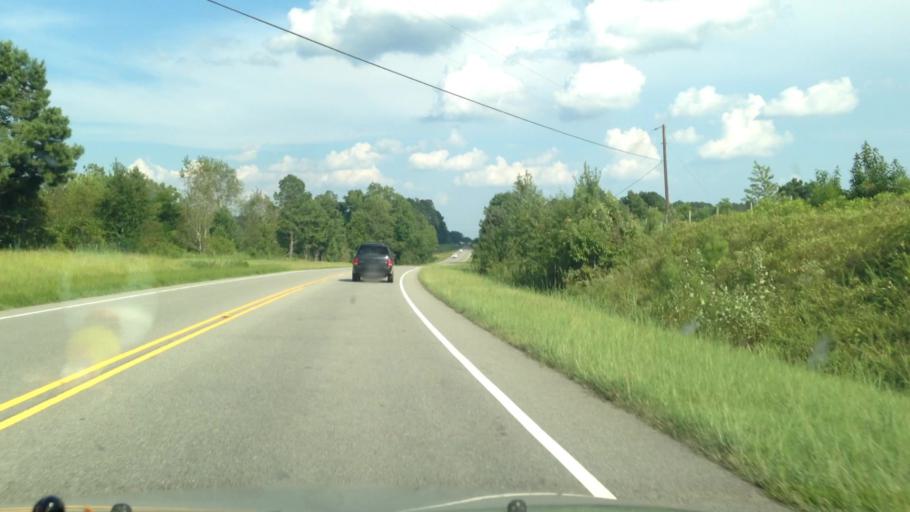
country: US
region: North Carolina
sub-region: Harnett County
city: Lillington
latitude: 35.4180
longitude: -78.8775
